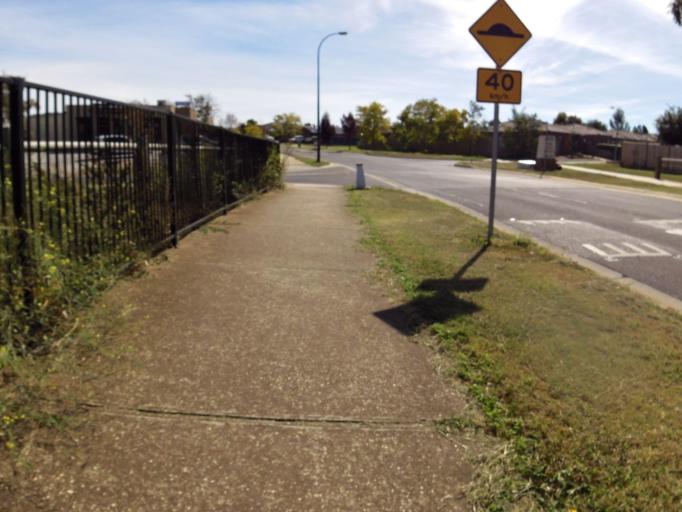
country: AU
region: Victoria
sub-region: Melton
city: Melton West
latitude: -37.6641
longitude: 144.5699
